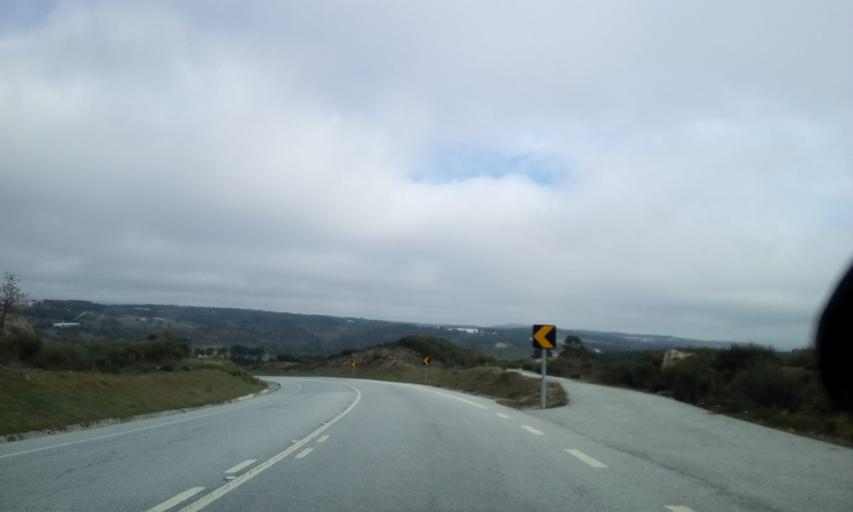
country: PT
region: Guarda
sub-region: Aguiar da Beira
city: Aguiar da Beira
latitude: 40.7704
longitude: -7.5033
